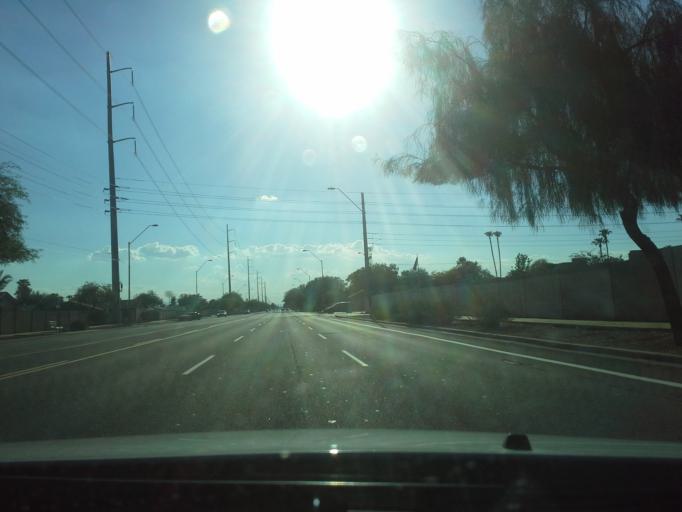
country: US
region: Arizona
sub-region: Maricopa County
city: Glendale
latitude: 33.6547
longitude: -112.1245
